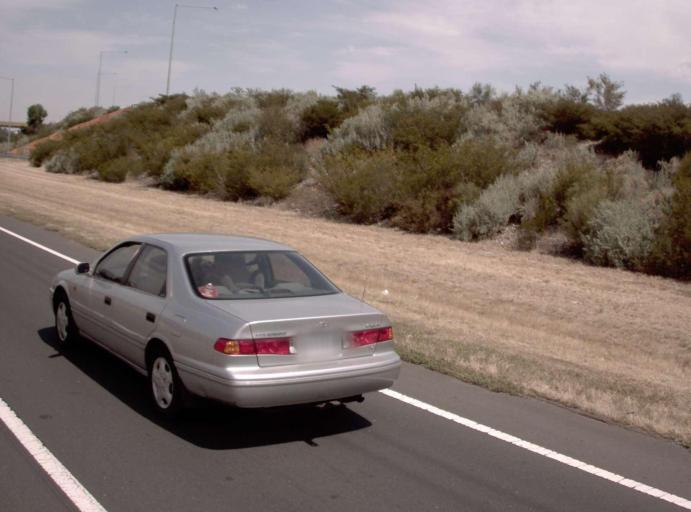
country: AU
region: Victoria
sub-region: Brimbank
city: Derrimut
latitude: -37.7920
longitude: 144.7887
